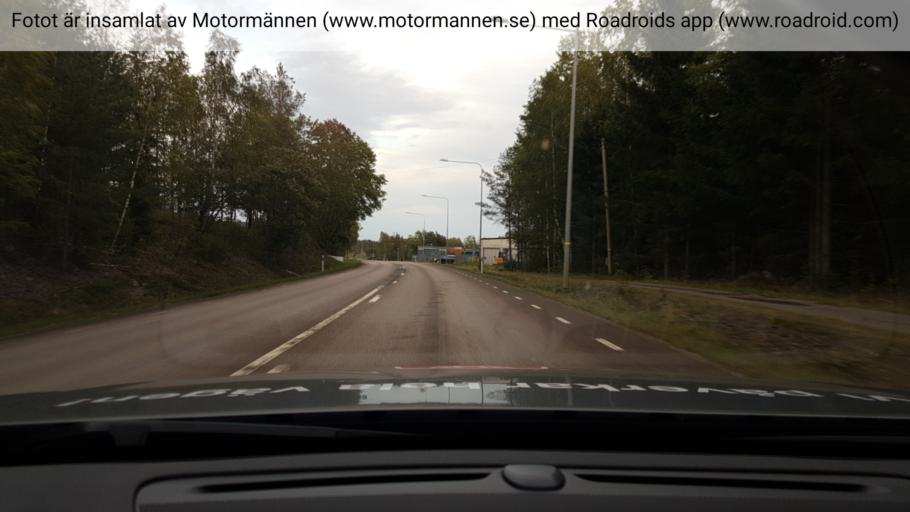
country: SE
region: Vaestra Goetaland
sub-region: Amals Kommun
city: Amal
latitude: 59.0572
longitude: 12.6600
